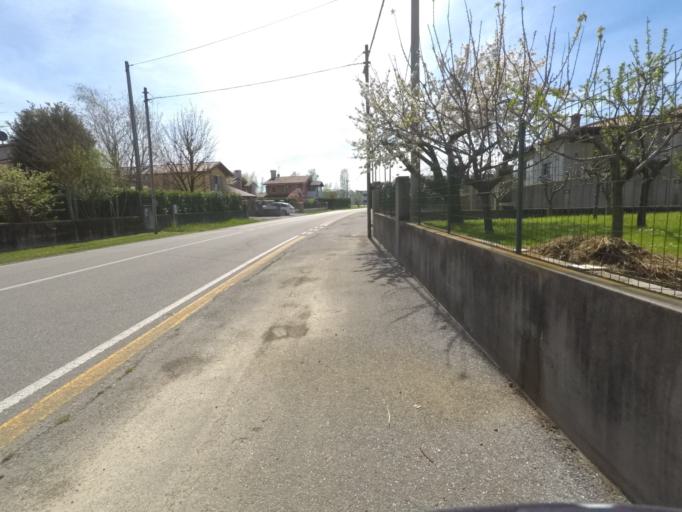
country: IT
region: Friuli Venezia Giulia
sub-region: Provincia di Pordenone
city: Orcenico Inferiore
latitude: 45.9510
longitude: 12.7853
